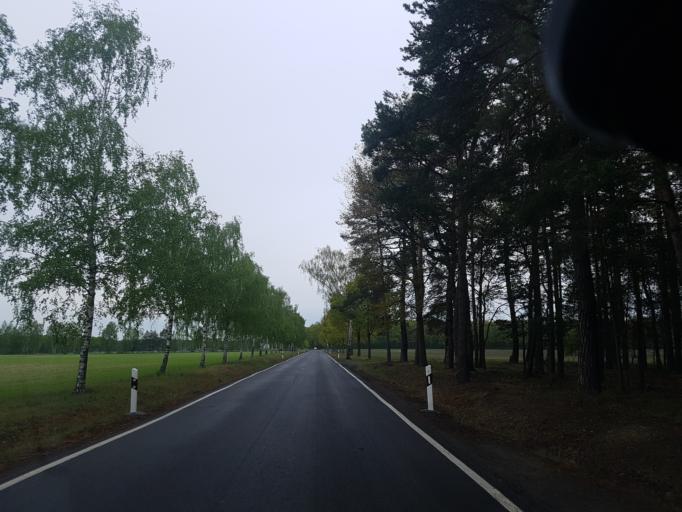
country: DE
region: Brandenburg
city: Spremberg
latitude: 51.6362
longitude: 14.4333
